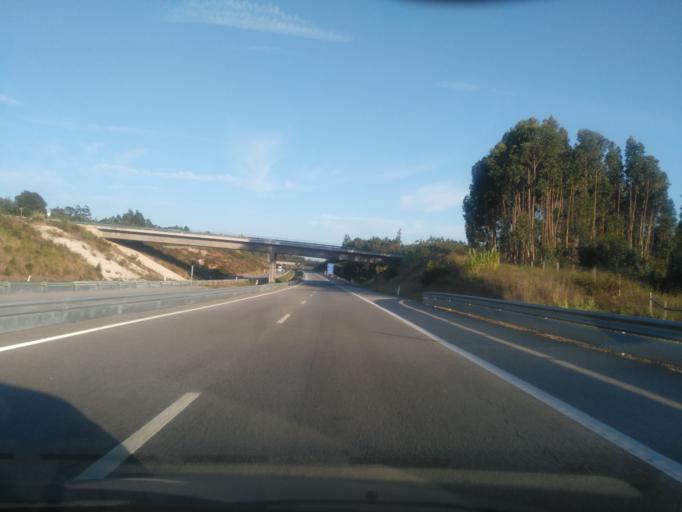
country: PT
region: Coimbra
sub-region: Figueira da Foz
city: Alhadas
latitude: 40.1767
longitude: -8.8001
